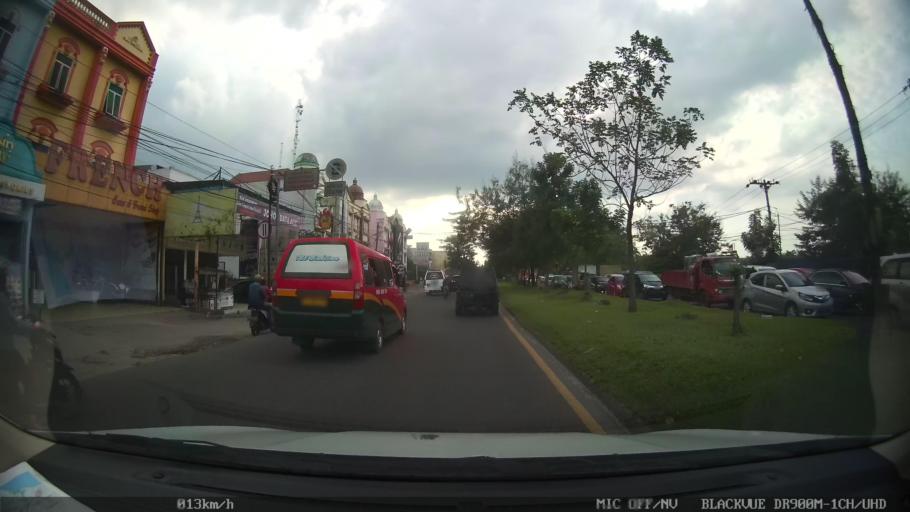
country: ID
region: North Sumatra
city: Deli Tua
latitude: 3.5414
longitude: 98.6630
